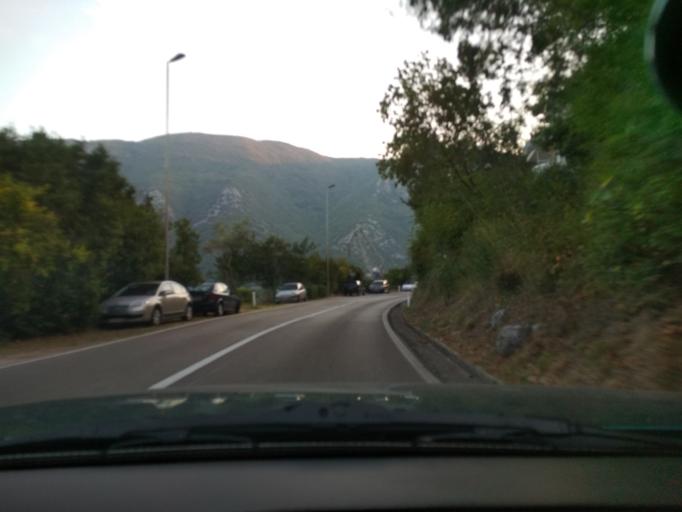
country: ME
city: Lipci
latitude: 42.4997
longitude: 18.6607
